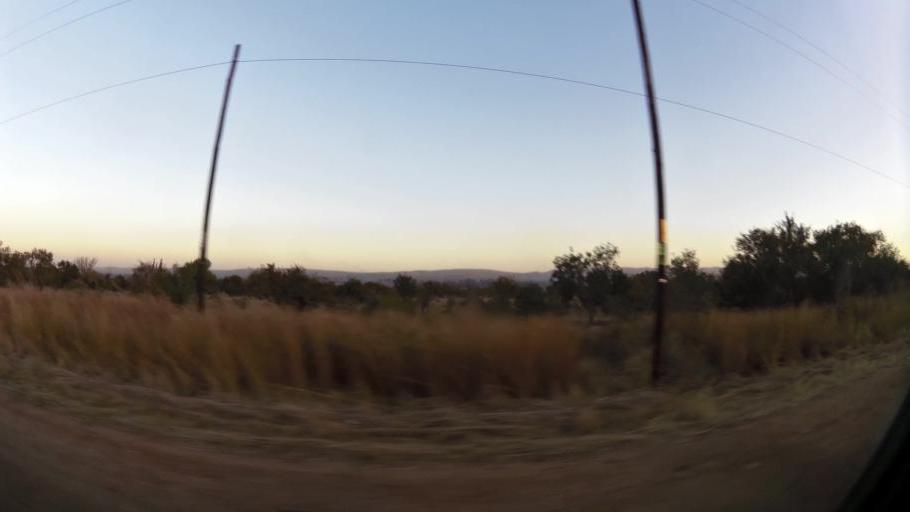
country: ZA
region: North-West
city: Ga-Rankuwa
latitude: -25.6205
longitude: 28.0341
